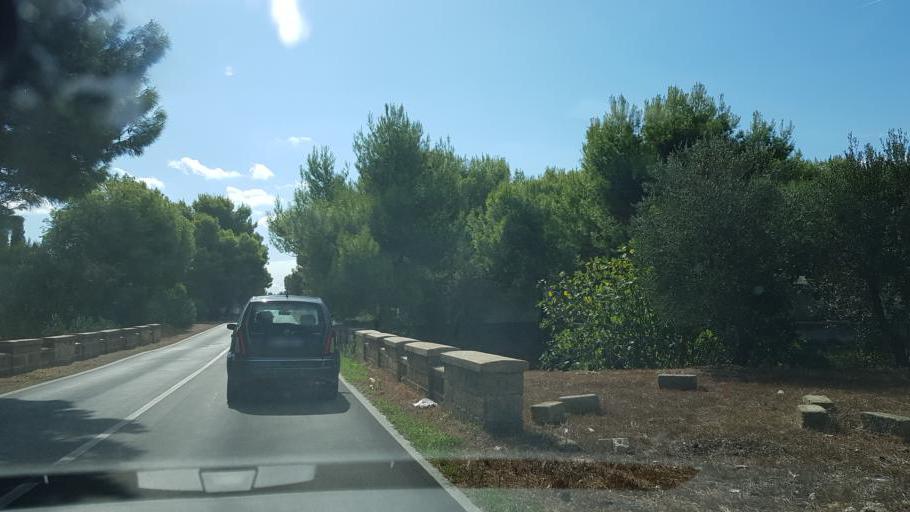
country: IT
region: Apulia
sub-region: Provincia di Lecce
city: Porto Cesareo
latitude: 40.2430
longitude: 17.9147
